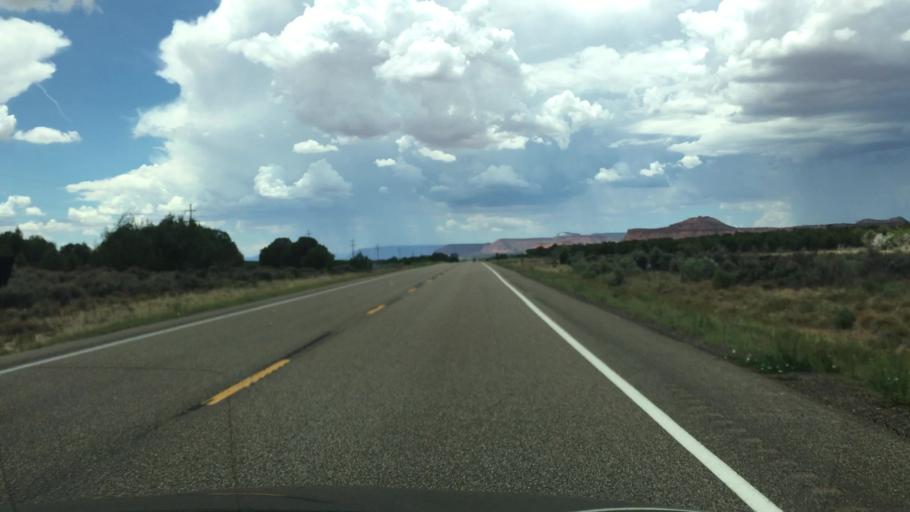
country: US
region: Utah
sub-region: Kane County
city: Kanab
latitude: 37.0405
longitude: -112.2537
